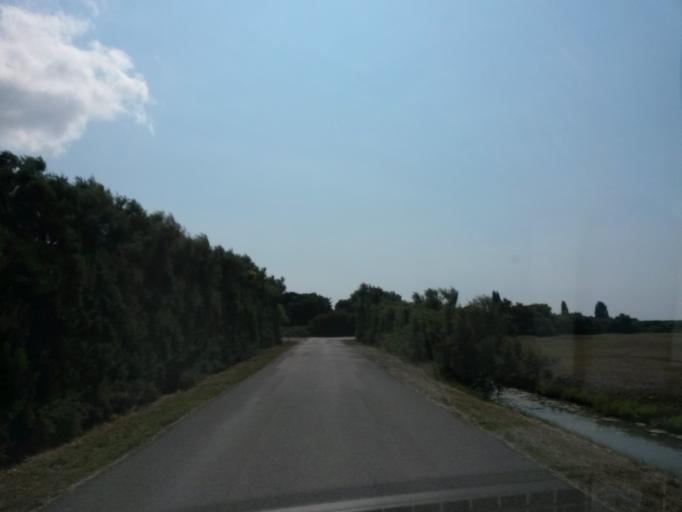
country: FR
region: Pays de la Loire
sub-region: Departement de la Vendee
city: Saint-Hilaire-de-Talmont
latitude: 46.4398
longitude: -1.6021
